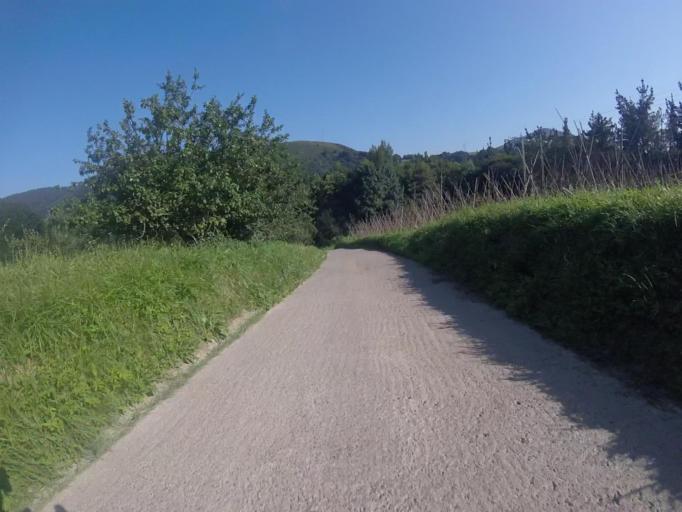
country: ES
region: Basque Country
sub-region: Provincia de Guipuzcoa
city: Astigarraga
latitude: 43.2561
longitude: -1.9398
